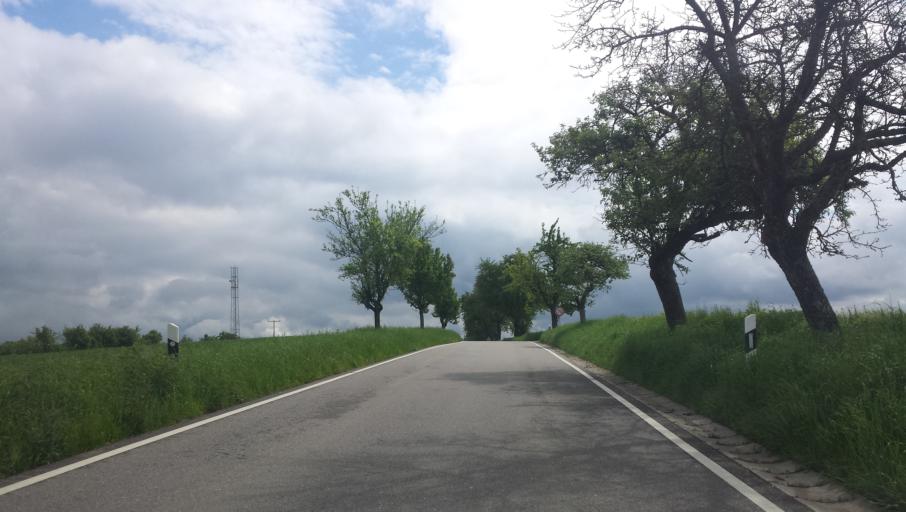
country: DE
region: Baden-Wuerttemberg
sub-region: Karlsruhe Region
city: Neckarbischofsheim
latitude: 49.2608
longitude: 8.9657
